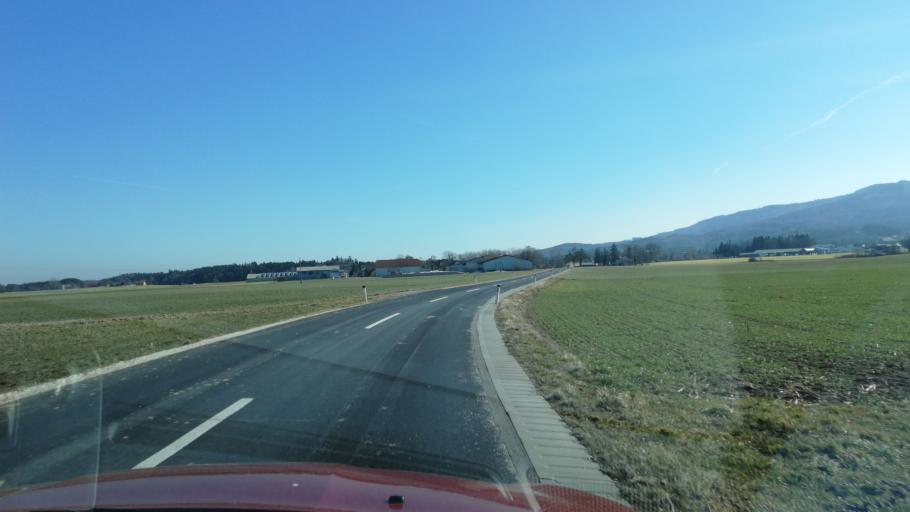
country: AT
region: Upper Austria
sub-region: Politischer Bezirk Vocklabruck
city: Aurach am Hongar
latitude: 47.9595
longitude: 13.6498
